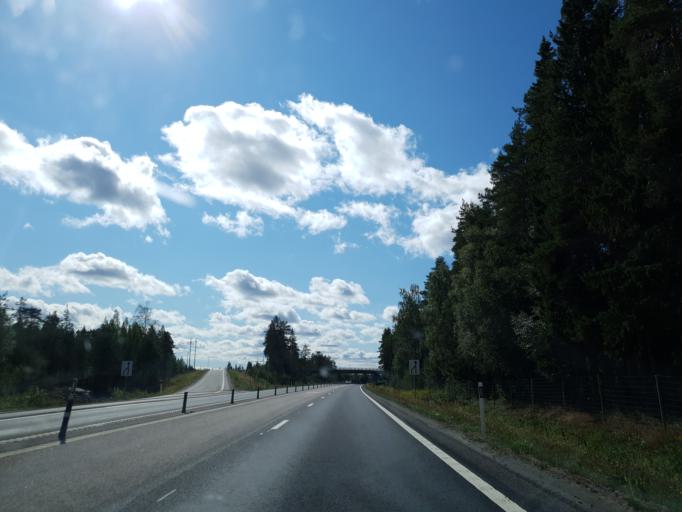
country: SE
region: Vaesterbotten
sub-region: Nordmalings Kommun
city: Nordmaling
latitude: 63.5391
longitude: 19.4045
